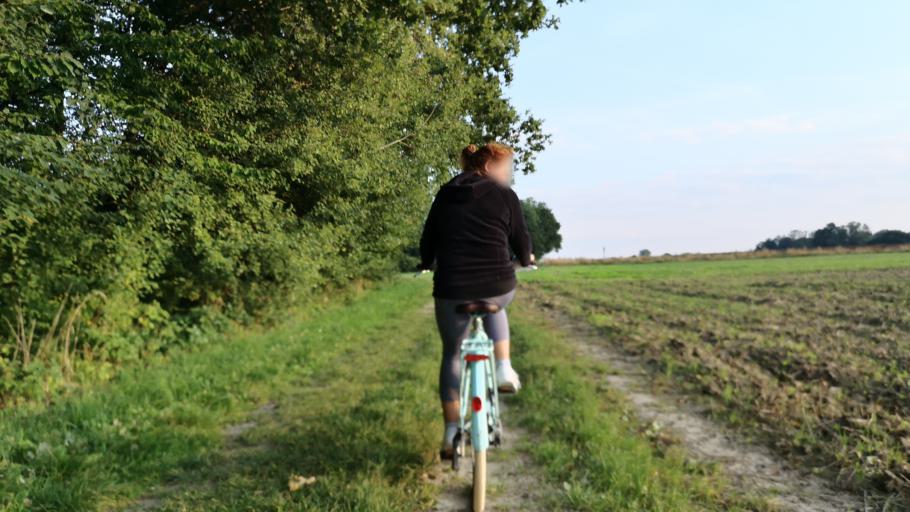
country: DE
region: Bavaria
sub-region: Upper Bavaria
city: Poing
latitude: 48.1629
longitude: 11.8222
